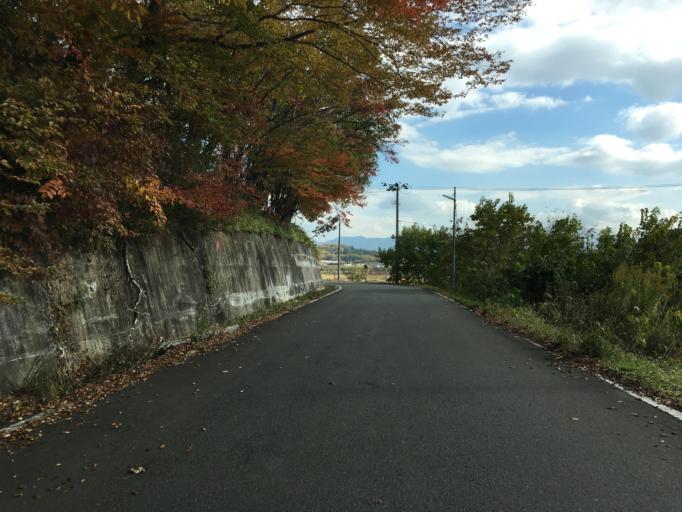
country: JP
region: Fukushima
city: Nihommatsu
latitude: 37.6366
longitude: 140.4710
